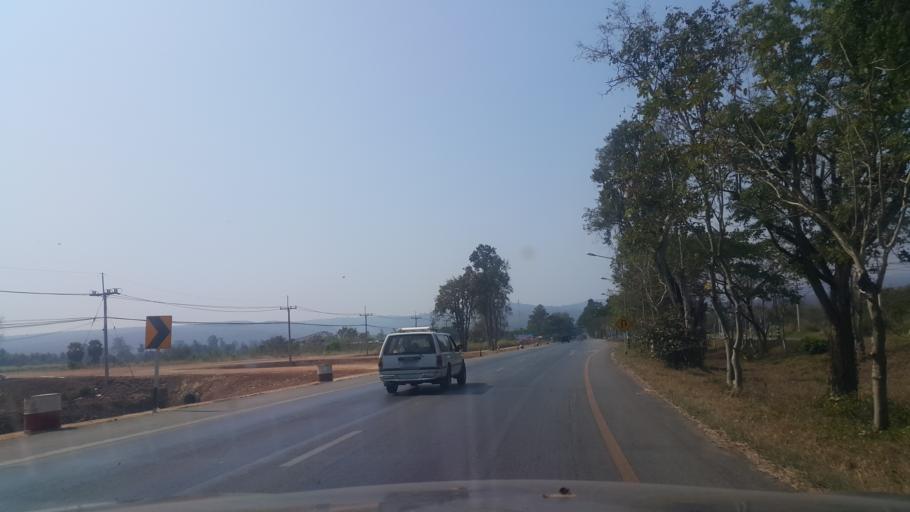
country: TH
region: Nakhon Ratchasima
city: Wang Nam Khiao
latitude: 14.5217
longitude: 101.9651
